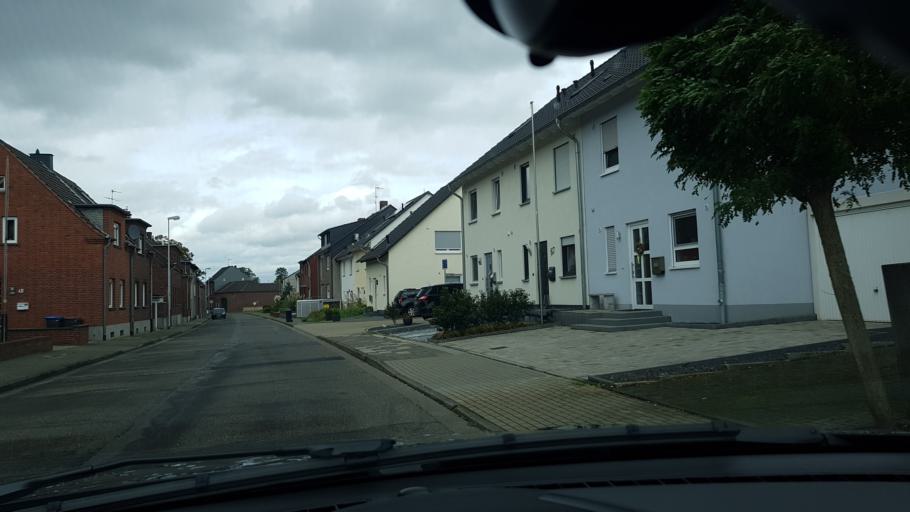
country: DE
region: North Rhine-Westphalia
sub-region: Regierungsbezirk Dusseldorf
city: Grevenbroich
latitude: 51.0620
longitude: 6.6257
